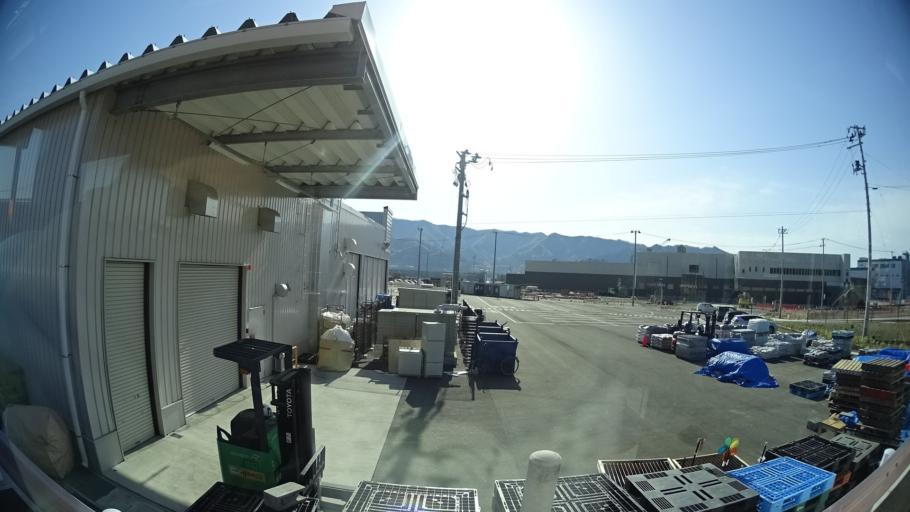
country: JP
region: Iwate
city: Ofunato
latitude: 39.0586
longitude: 141.7212
